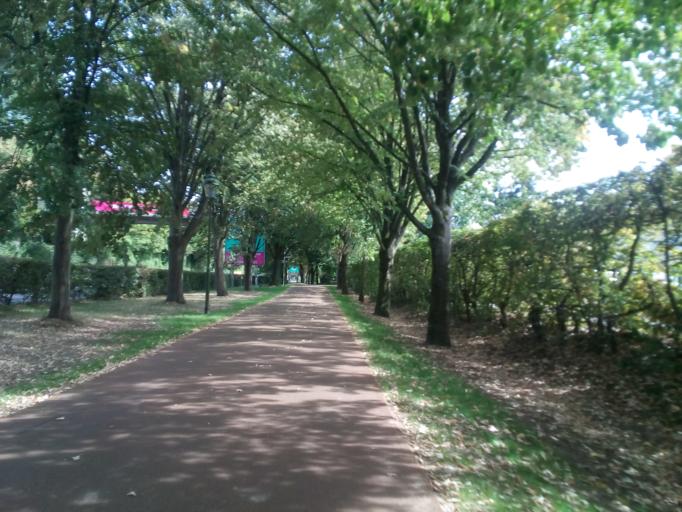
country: DE
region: Baden-Wuerttemberg
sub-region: Karlsruhe Region
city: Baden-Baden
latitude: 48.7809
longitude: 8.2073
